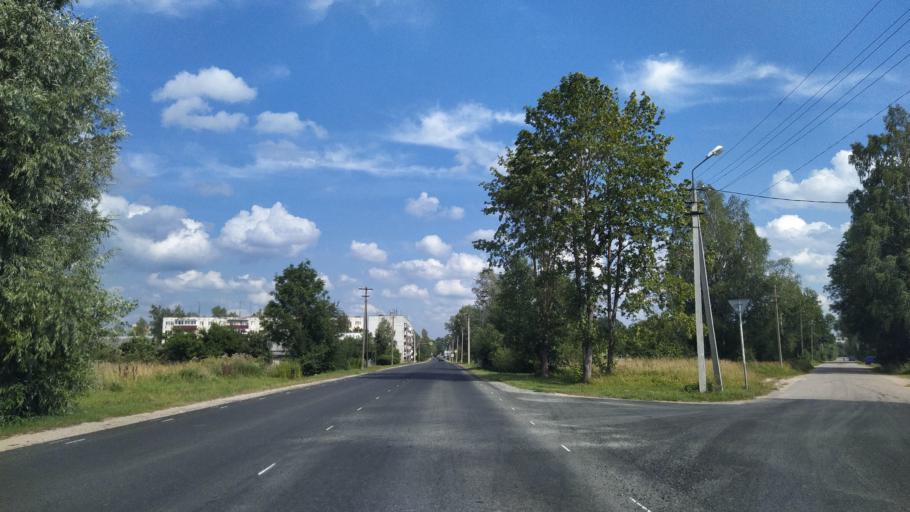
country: RU
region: Pskov
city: Porkhov
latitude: 57.7606
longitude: 29.5472
